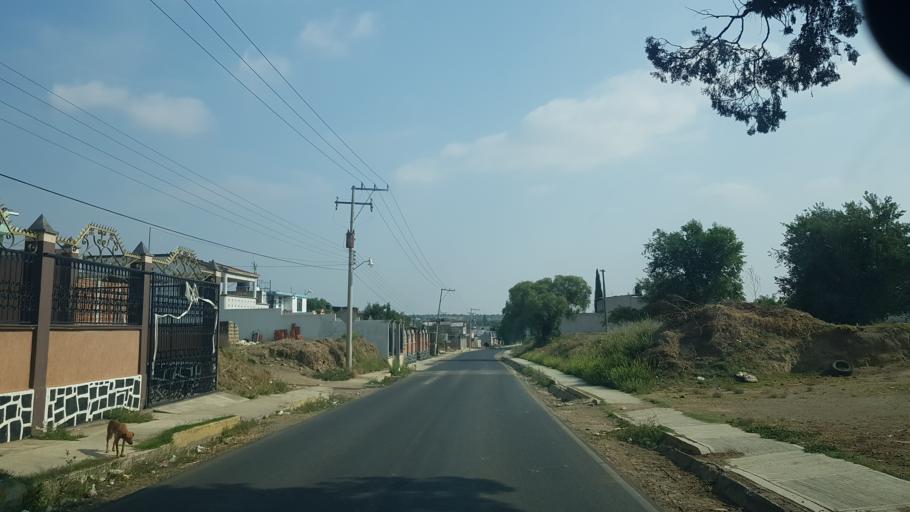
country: MX
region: Puebla
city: San Andres Calpan
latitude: 19.1175
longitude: -98.4254
